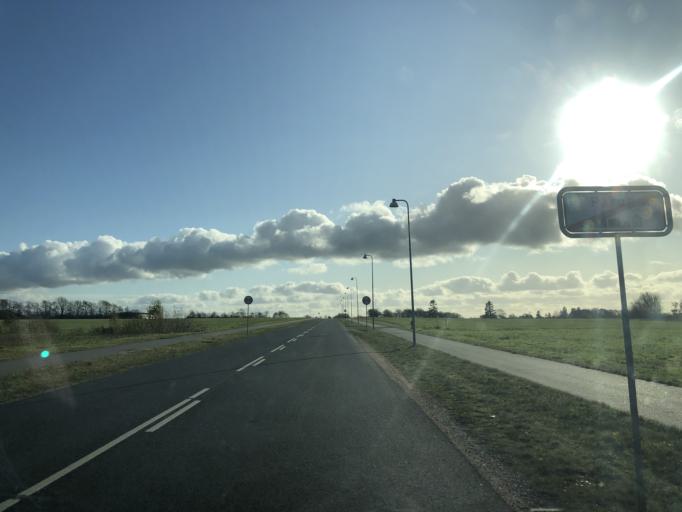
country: DK
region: Central Jutland
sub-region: Ikast-Brande Kommune
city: Bording Kirkeby
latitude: 56.1364
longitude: 9.3429
